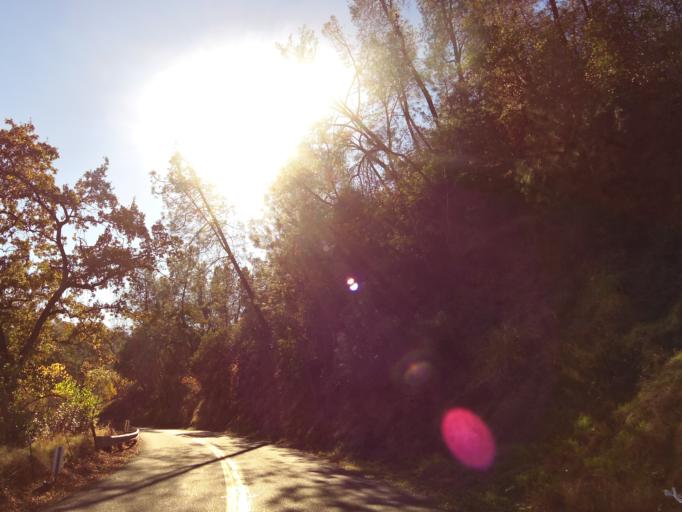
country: US
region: California
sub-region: Yolo County
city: Winters
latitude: 38.4784
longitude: -122.0306
